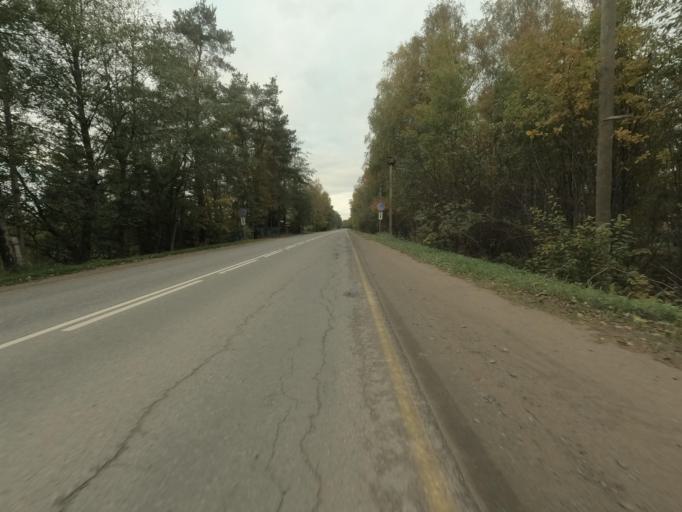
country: RU
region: Leningrad
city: Pavlovo
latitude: 59.7811
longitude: 30.9714
